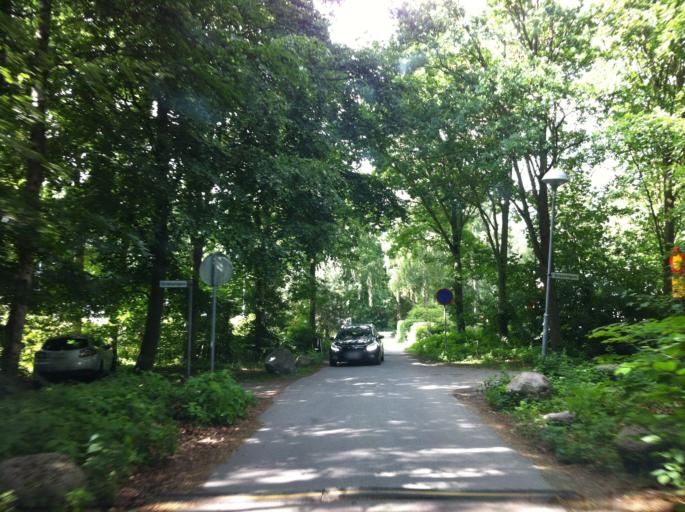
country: SE
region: Skane
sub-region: Ystads Kommun
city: Ystad
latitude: 55.4304
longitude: 13.8612
